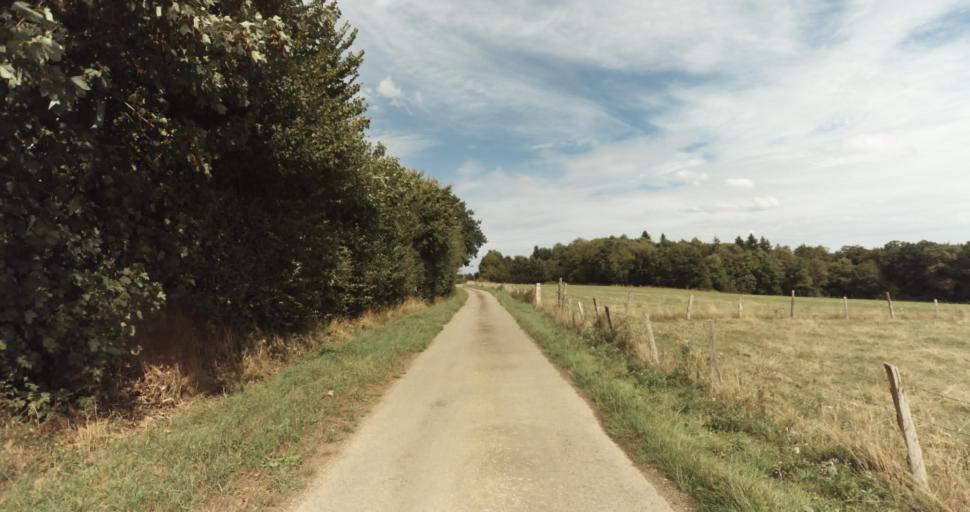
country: FR
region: Lower Normandy
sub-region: Departement du Calvados
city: Orbec
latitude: 48.9270
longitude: 0.3817
